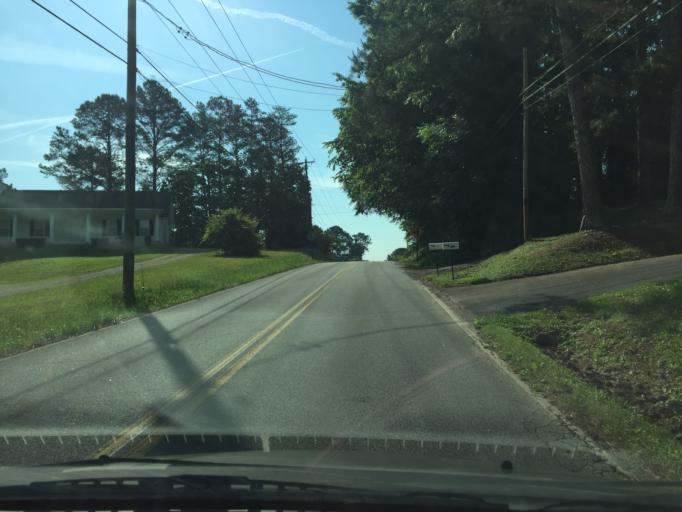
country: US
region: Tennessee
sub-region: Hamilton County
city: Collegedale
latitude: 35.0599
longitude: -85.0194
